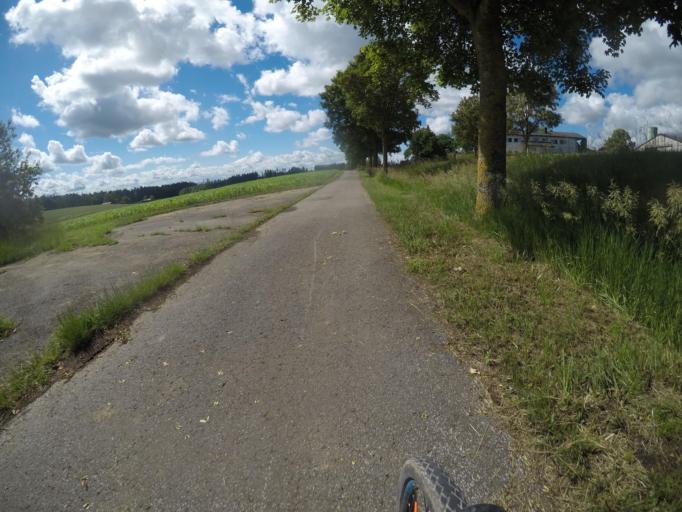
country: DE
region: Baden-Wuerttemberg
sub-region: Regierungsbezirk Stuttgart
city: Unterjettingen
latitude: 48.5555
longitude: 8.7824
